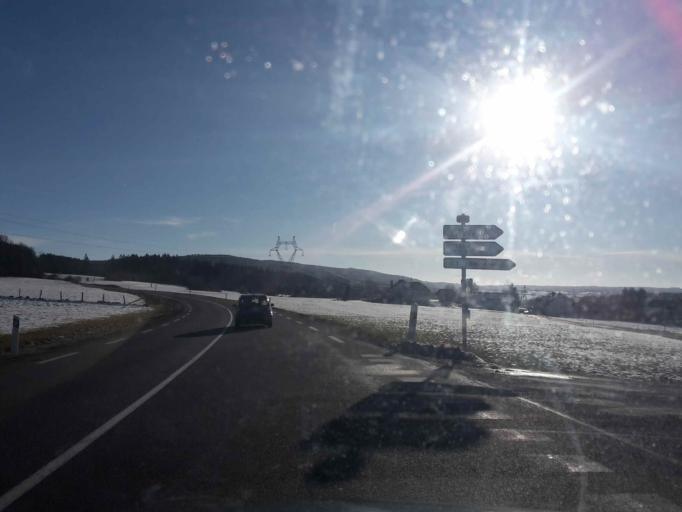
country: FR
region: Franche-Comte
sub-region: Departement du Doubs
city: Doubs
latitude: 47.0200
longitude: 6.3256
